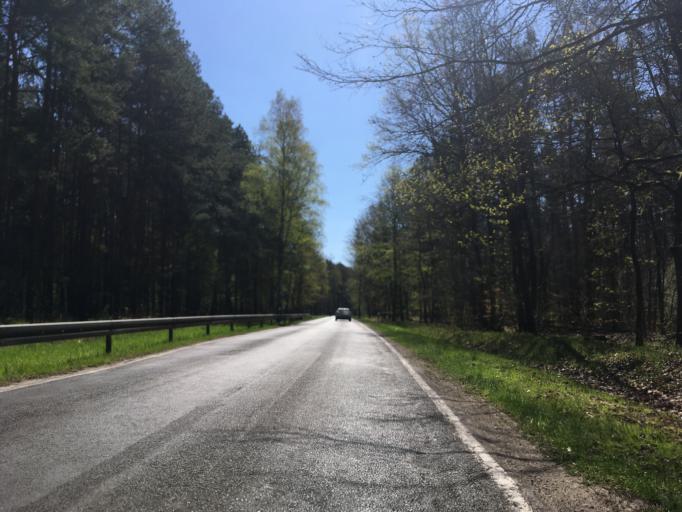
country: DE
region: Brandenburg
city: Bernau bei Berlin
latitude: 52.7144
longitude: 13.5771
